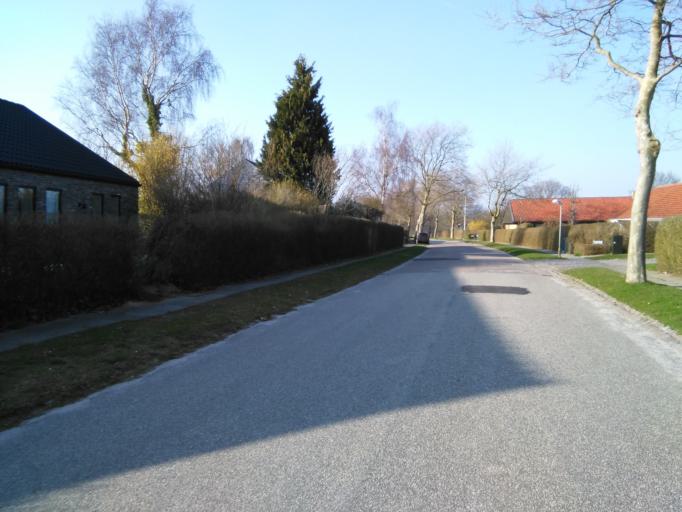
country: DK
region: Central Jutland
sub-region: Arhus Kommune
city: Beder
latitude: 56.0650
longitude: 10.2118
